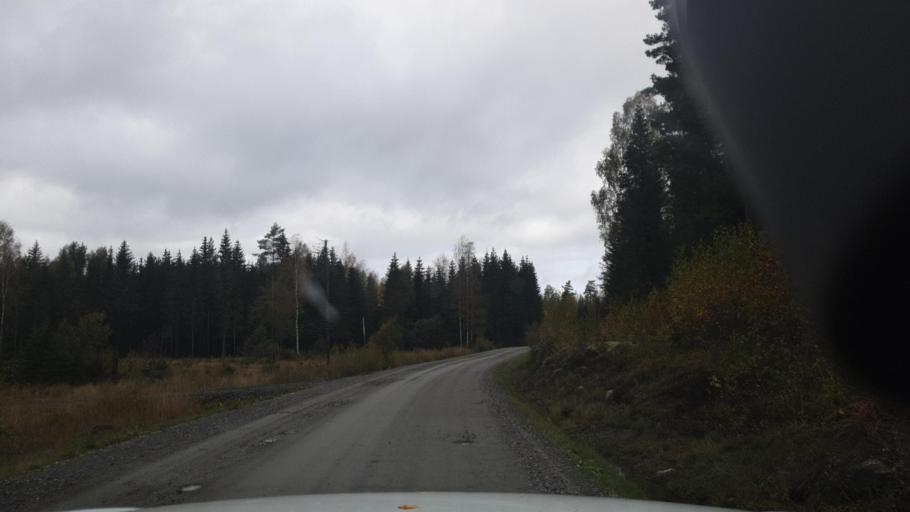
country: SE
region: Vaermland
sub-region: Karlstads Kommun
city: Edsvalla
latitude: 59.4480
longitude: 13.1556
